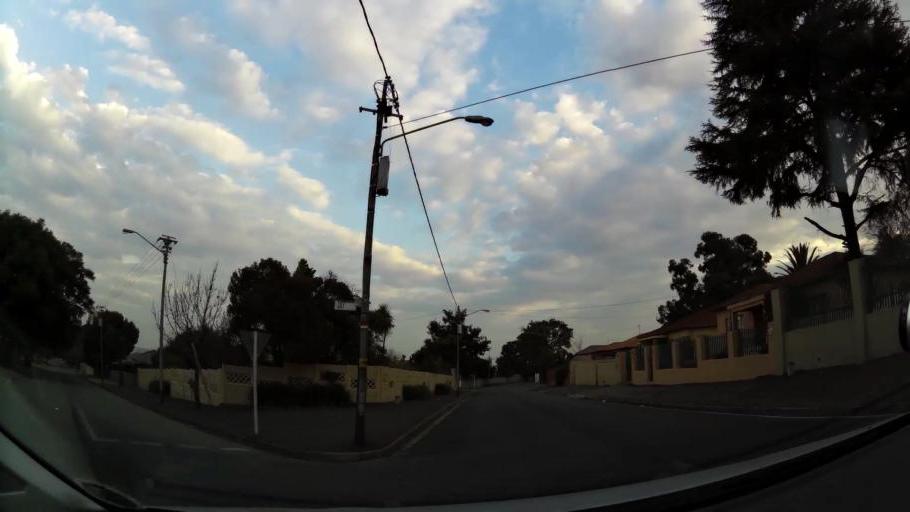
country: ZA
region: Gauteng
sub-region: Ekurhuleni Metropolitan Municipality
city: Germiston
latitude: -26.1881
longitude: 28.1526
